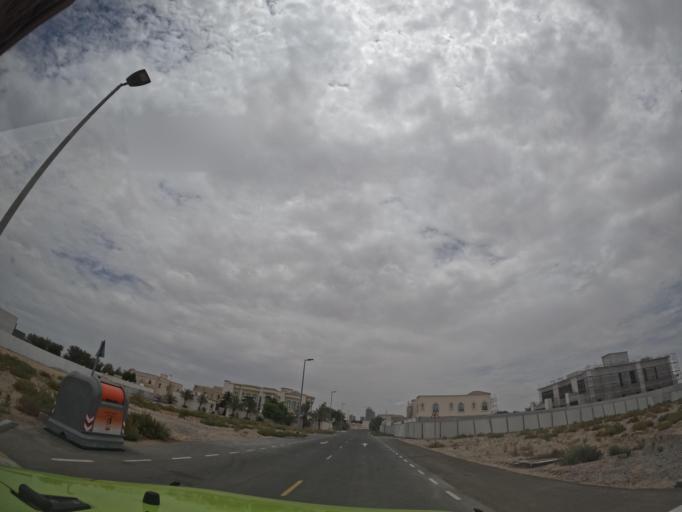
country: AE
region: Dubai
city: Dubai
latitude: 25.1311
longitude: 55.3582
